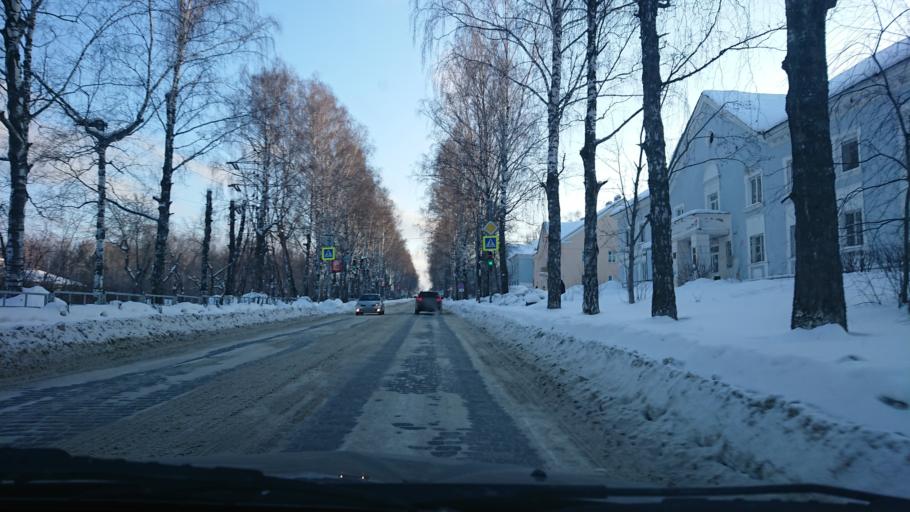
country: RU
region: Sverdlovsk
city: Degtyarsk
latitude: 56.6972
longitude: 60.0879
